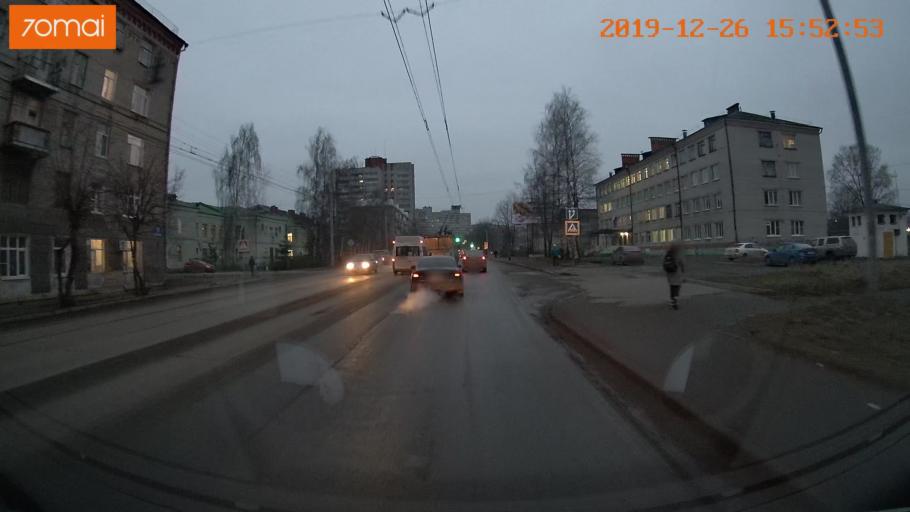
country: RU
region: Jaroslavl
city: Rybinsk
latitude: 58.0501
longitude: 38.8240
